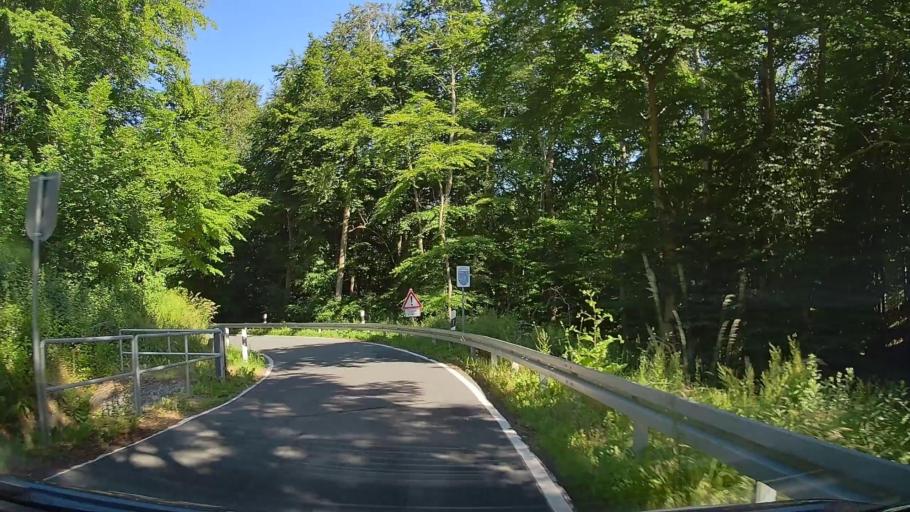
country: DE
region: Lower Saxony
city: Vahlbruch
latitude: 51.9771
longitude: 9.3554
